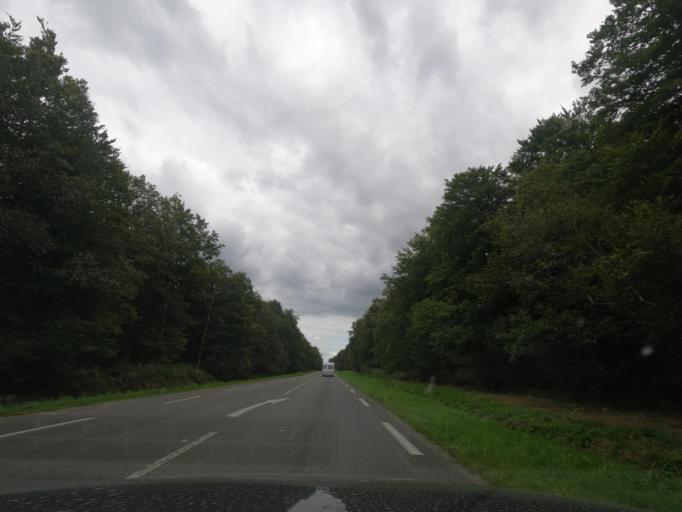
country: FR
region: Brittany
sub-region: Departement d'Ille-et-Vilaine
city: Landean
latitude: 48.4005
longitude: -1.1596
